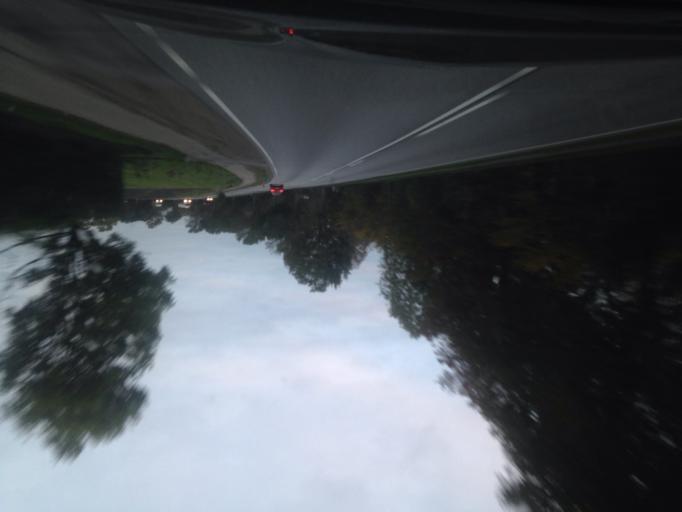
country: DK
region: Zealand
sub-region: Solrod Kommune
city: Havdrup
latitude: 55.5555
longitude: 12.1513
